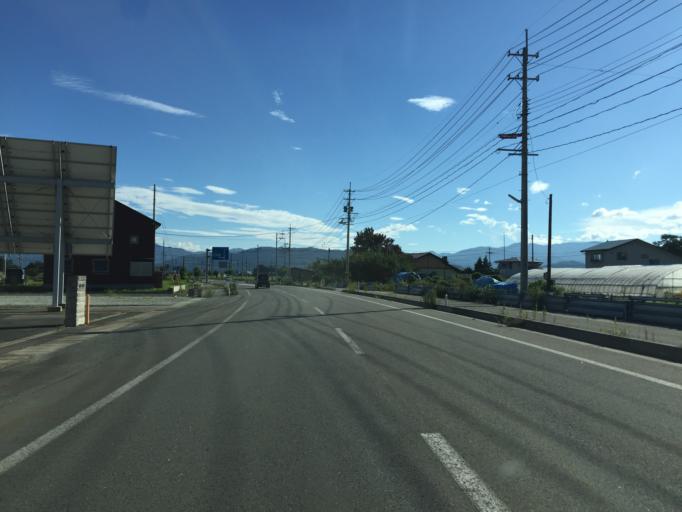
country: JP
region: Yamagata
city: Yonezawa
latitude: 37.9489
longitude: 140.1075
